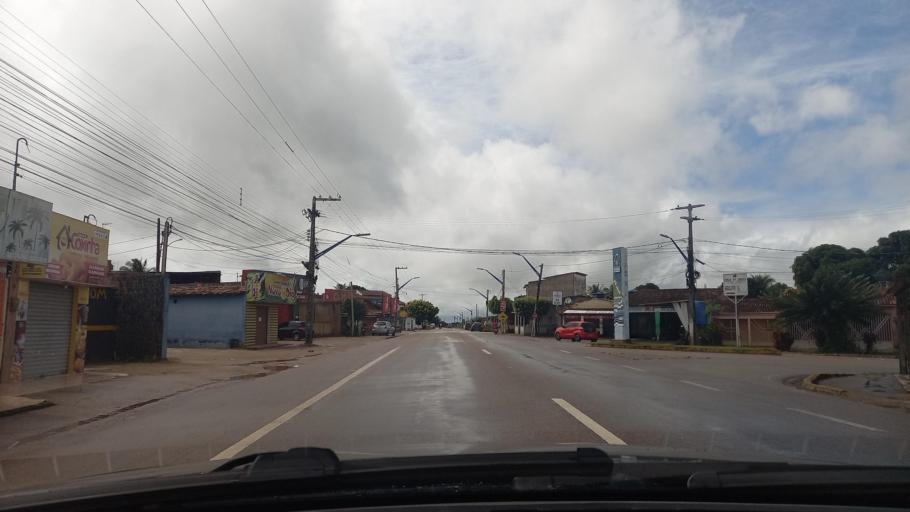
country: BR
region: Alagoas
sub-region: Limoeiro De Anadia
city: Limoeiro de Anadia
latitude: -9.7583
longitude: -36.5576
